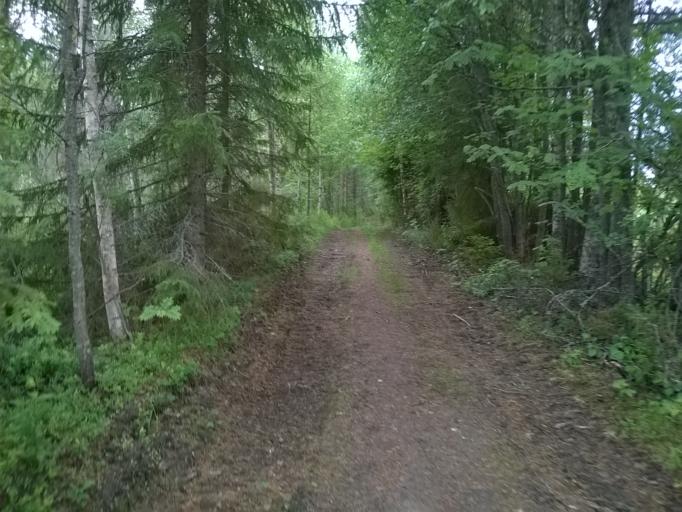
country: FI
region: Kainuu
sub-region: Kehys-Kainuu
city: Kuhmo
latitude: 64.1276
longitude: 29.4015
